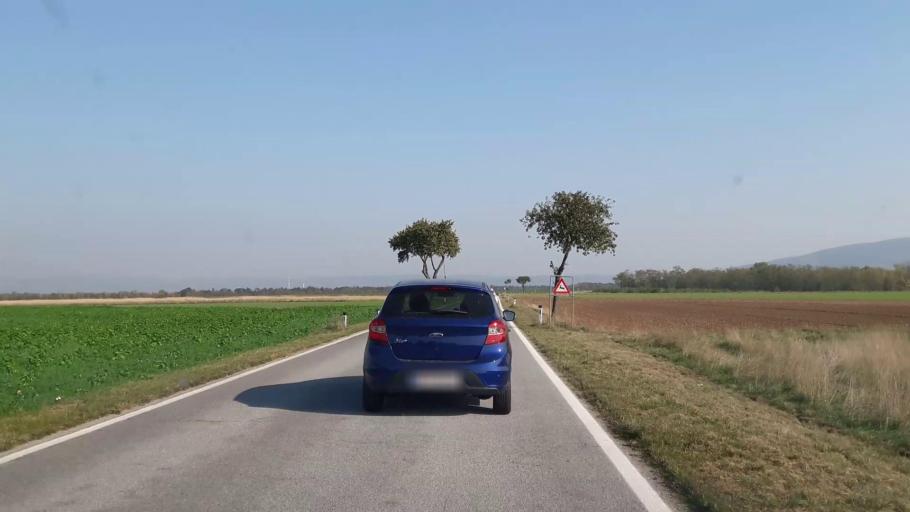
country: AT
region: Lower Austria
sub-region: Politischer Bezirk Ganserndorf
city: Marchegg
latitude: 48.2222
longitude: 16.9085
